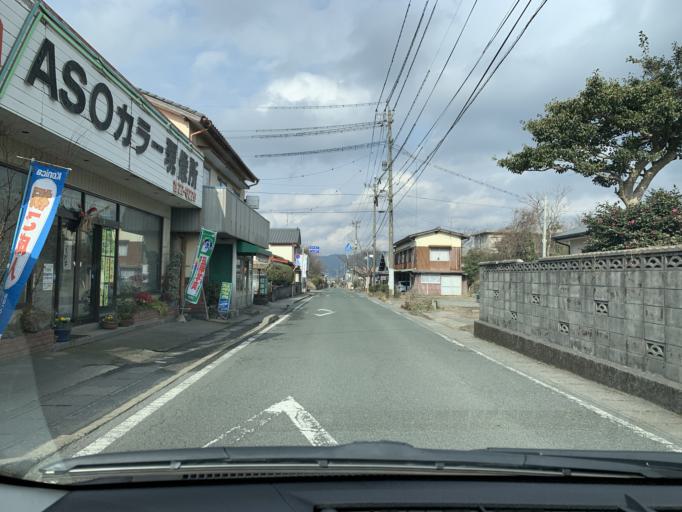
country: JP
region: Kumamoto
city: Aso
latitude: 32.9406
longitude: 131.1154
